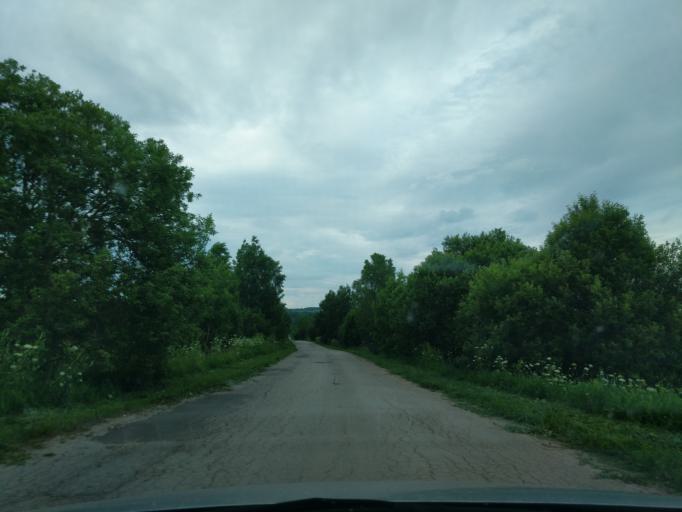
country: RU
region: Kaluga
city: Nikola-Lenivets
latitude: 54.7539
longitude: 35.6962
